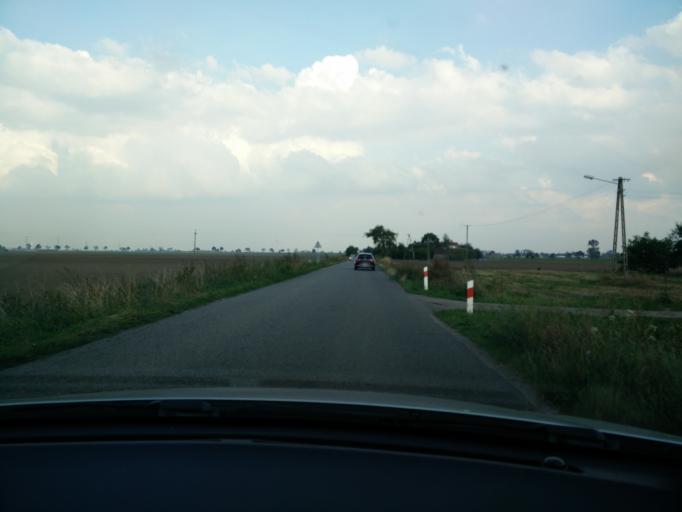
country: PL
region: Greater Poland Voivodeship
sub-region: Powiat wrzesinski
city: Wrzesnia
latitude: 52.2834
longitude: 17.5268
